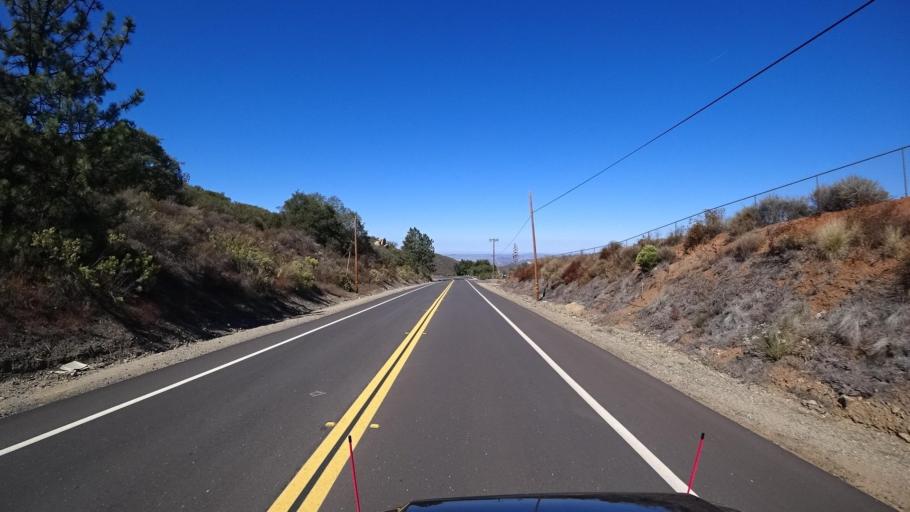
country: US
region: California
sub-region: San Diego County
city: Jamul
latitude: 32.7331
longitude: -116.7981
